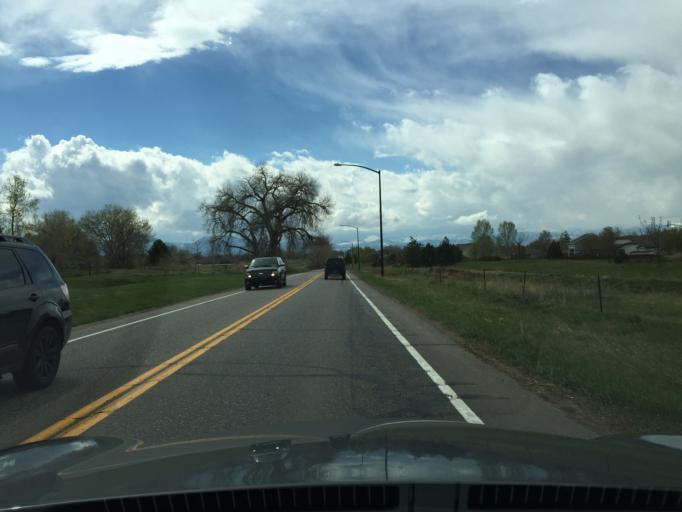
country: US
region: Colorado
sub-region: Boulder County
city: Lafayette
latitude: 40.0147
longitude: -105.0851
